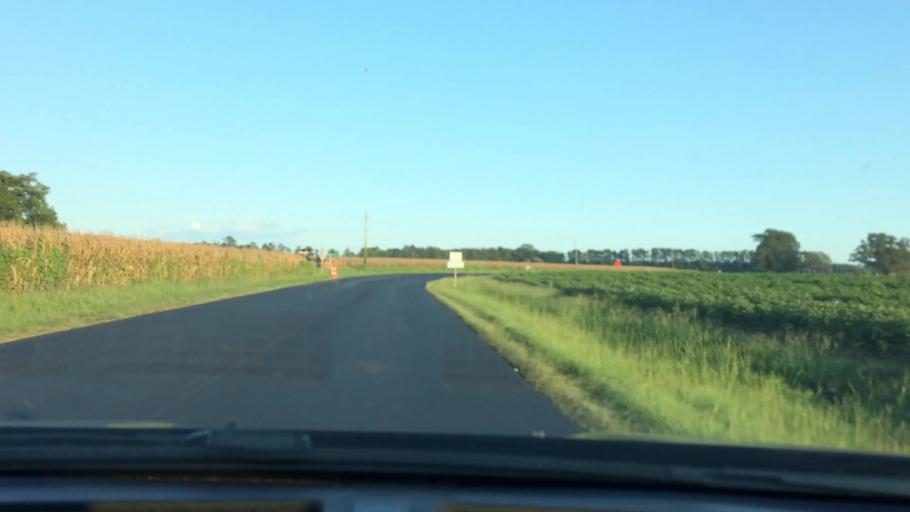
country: US
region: North Carolina
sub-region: Pitt County
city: Ayden
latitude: 35.4430
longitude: -77.4547
